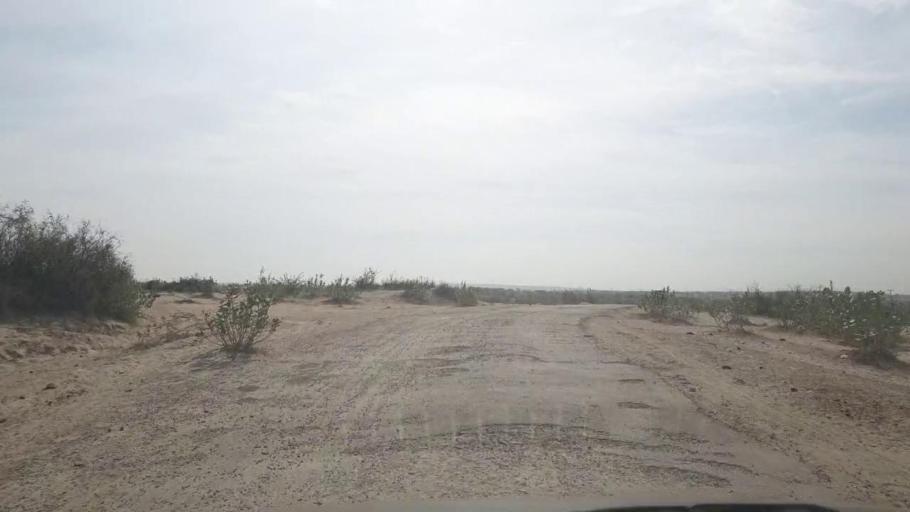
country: PK
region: Sindh
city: Umarkot
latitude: 25.2891
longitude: 69.7402
